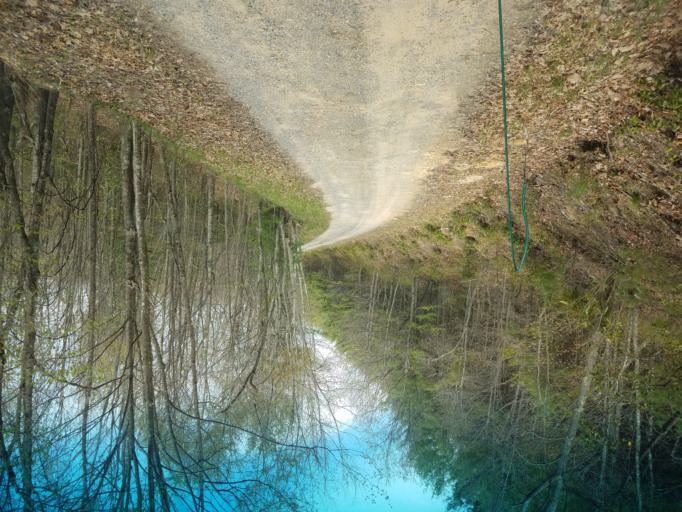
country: US
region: Virginia
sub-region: Smyth County
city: Marion
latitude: 36.7874
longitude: -81.4610
